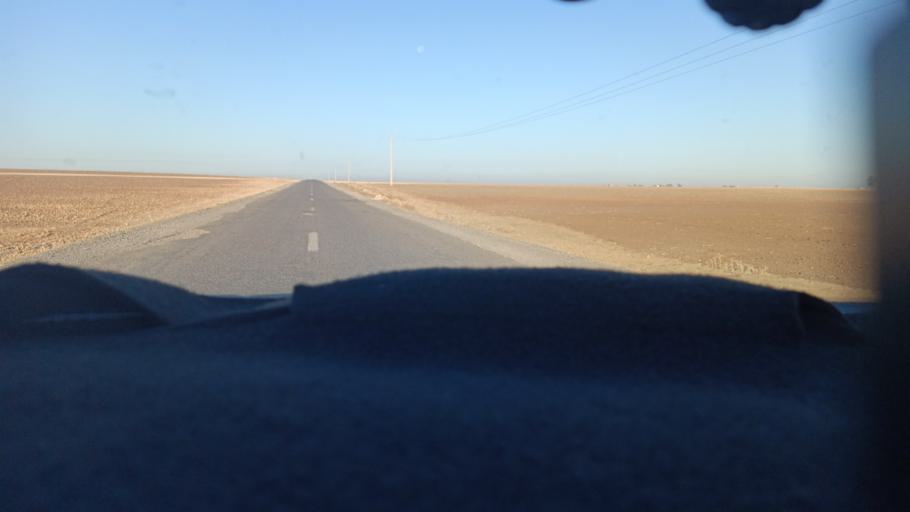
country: MA
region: Doukkala-Abda
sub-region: Safi
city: Youssoufia
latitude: 32.3719
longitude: -8.6357
